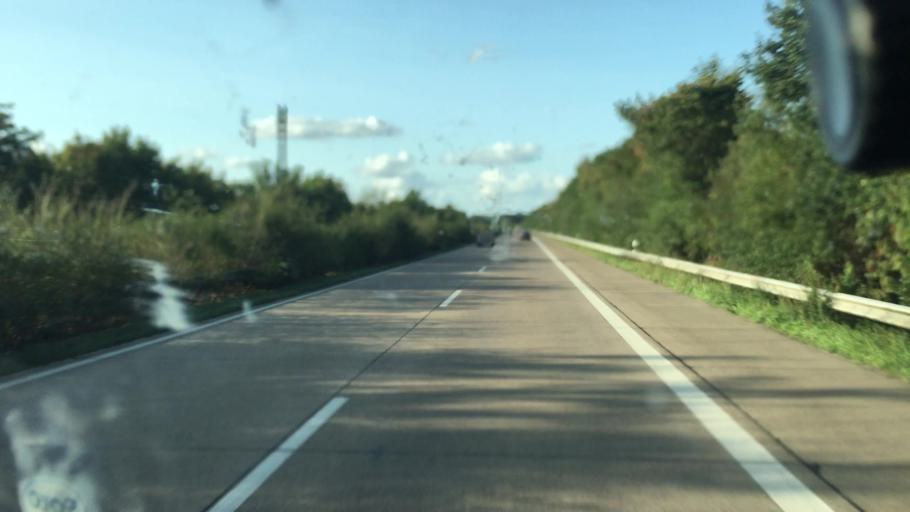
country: DE
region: Lower Saxony
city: Sande
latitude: 53.4642
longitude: 8.0177
